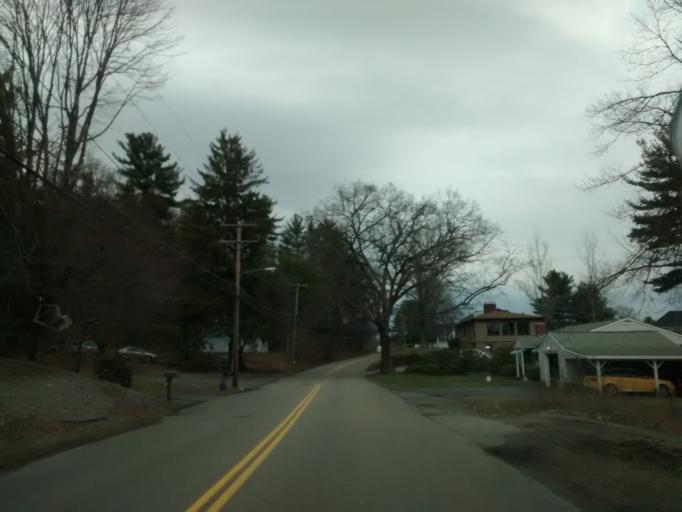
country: US
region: Massachusetts
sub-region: Worcester County
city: Grafton
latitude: 42.1916
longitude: -71.6997
